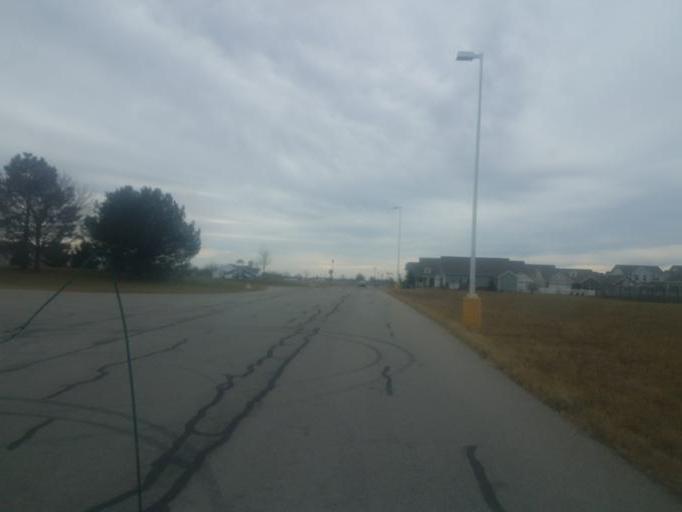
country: US
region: Ohio
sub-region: Marion County
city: Marion
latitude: 40.5783
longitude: -83.0704
